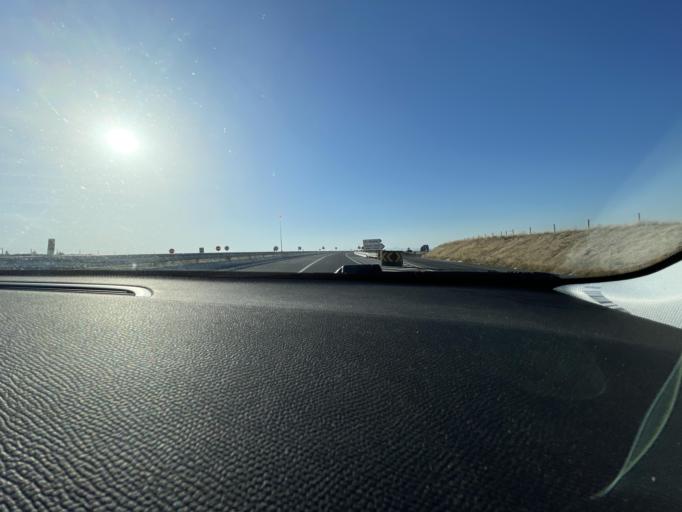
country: ES
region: Castille and Leon
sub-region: Provincia de Salamanca
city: Fuentes de Onoro
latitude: 40.6141
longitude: -6.8216
